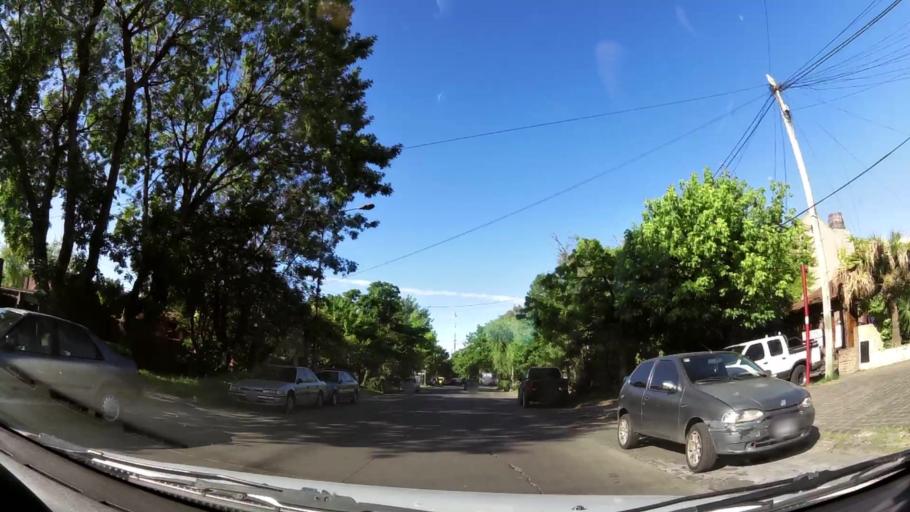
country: AR
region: Buenos Aires
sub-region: Partido de San Isidro
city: San Isidro
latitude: -34.4631
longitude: -58.5092
